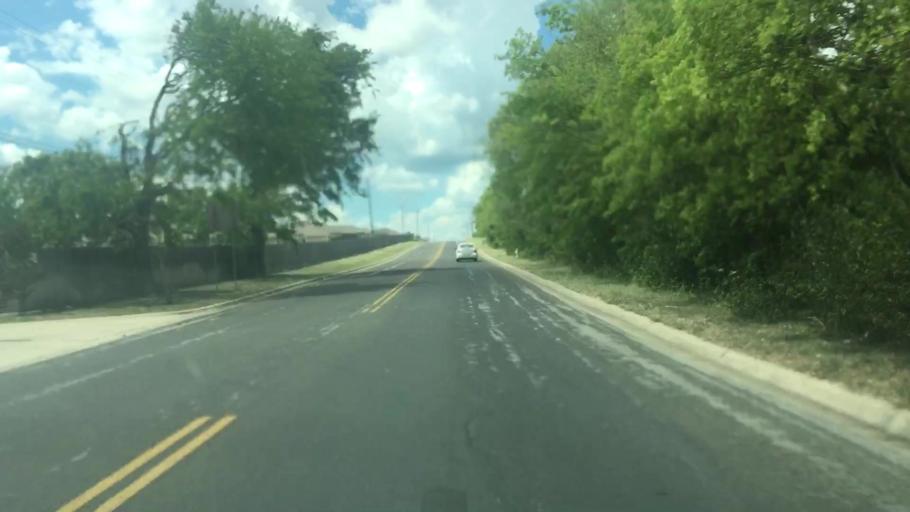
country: US
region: Texas
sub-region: Bell County
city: Temple
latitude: 31.1155
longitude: -97.3595
